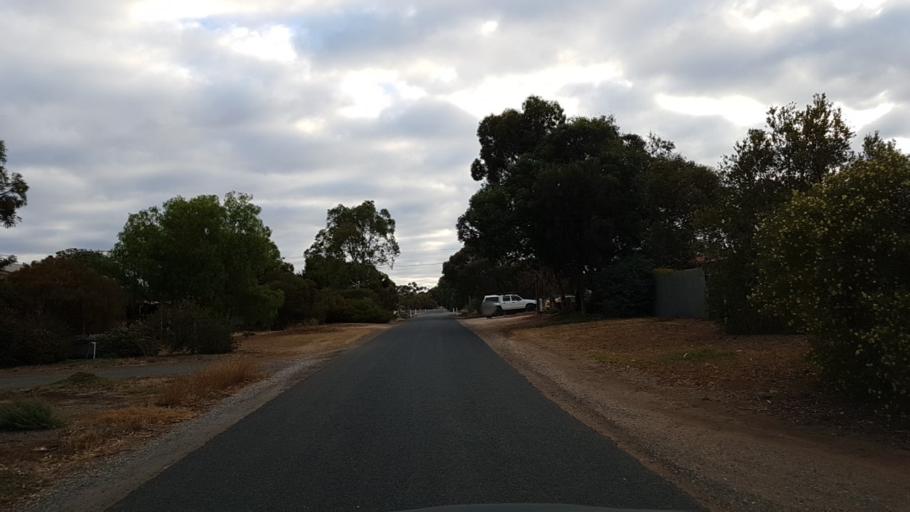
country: AU
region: South Australia
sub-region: Mount Barker
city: Callington
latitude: -35.1161
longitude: 139.0364
